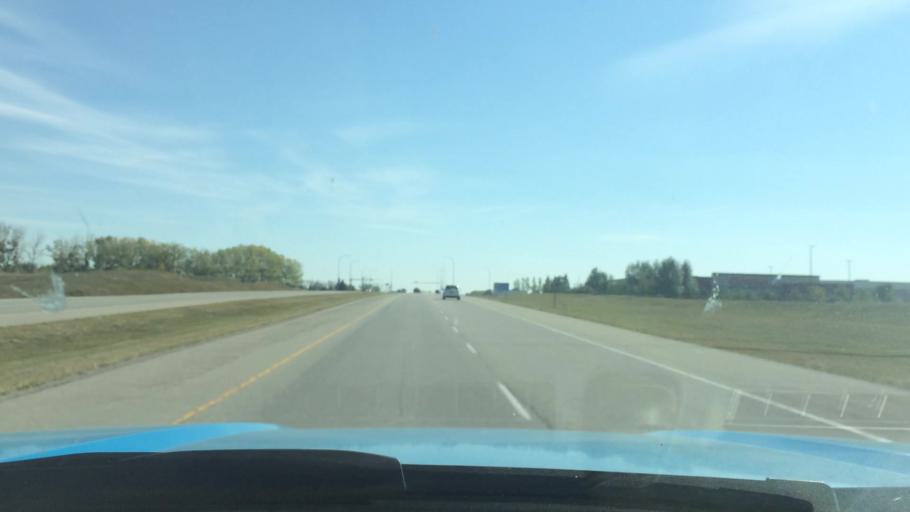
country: CA
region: Alberta
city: Airdrie
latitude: 51.2124
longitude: -113.9877
